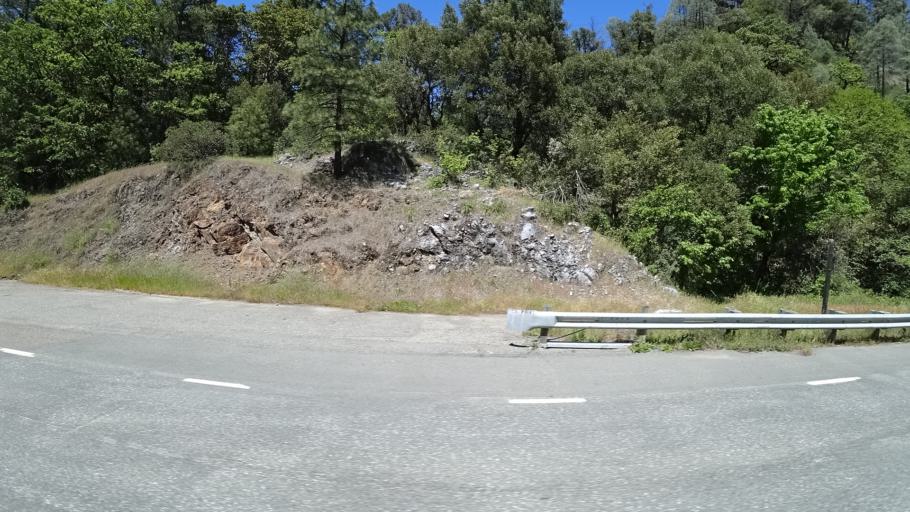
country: US
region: California
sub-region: Trinity County
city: Hayfork
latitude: 40.7392
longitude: -123.2446
